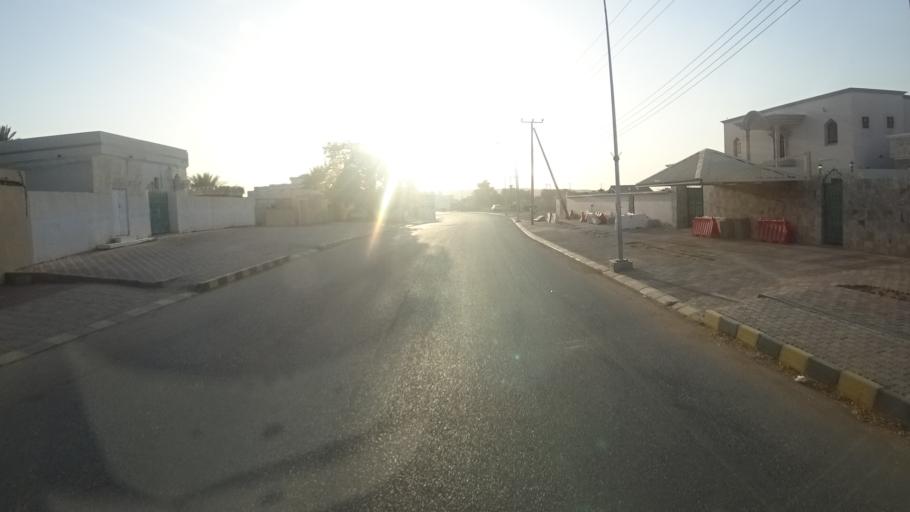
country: OM
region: Ash Sharqiyah
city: Badiyah
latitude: 22.5026
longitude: 58.7461
